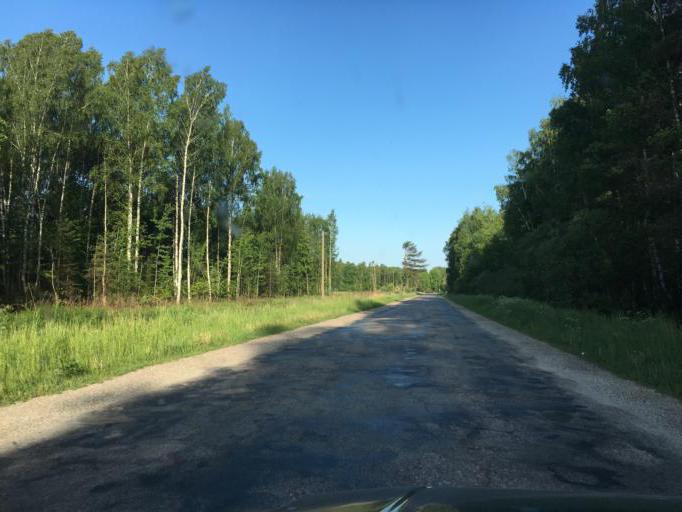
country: LV
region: Jelgava
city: Jelgava
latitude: 56.6553
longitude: 23.6054
